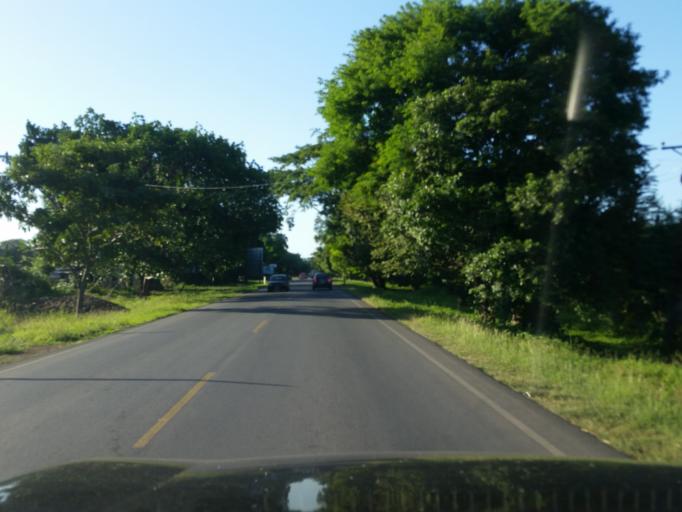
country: NI
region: Rivas
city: Potosi
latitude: 11.4697
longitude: -85.8564
